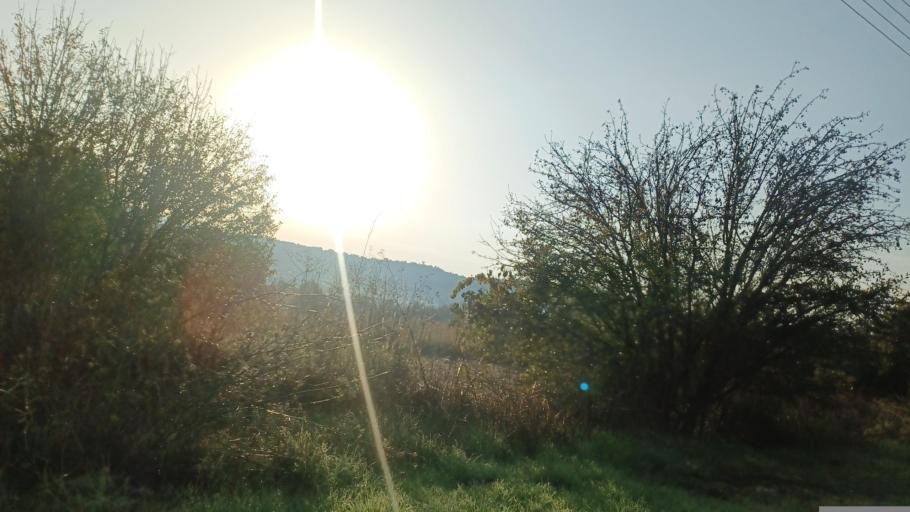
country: CY
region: Pafos
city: Tala
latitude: 34.8885
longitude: 32.4853
